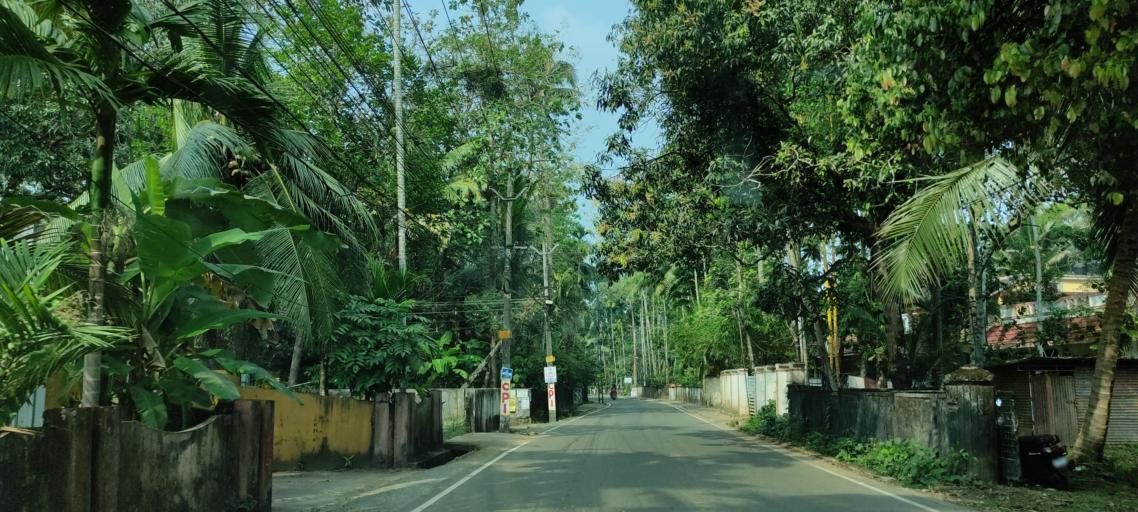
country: IN
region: Kerala
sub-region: Kottayam
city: Vaikam
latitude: 9.7529
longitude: 76.4023
